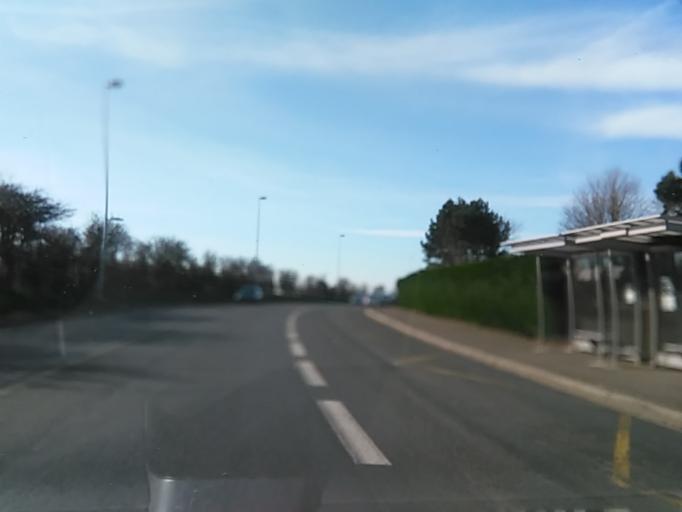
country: FR
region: Lower Normandy
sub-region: Departement de la Manche
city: Saint-Pair-sur-Mer
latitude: 48.8298
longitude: -1.5759
